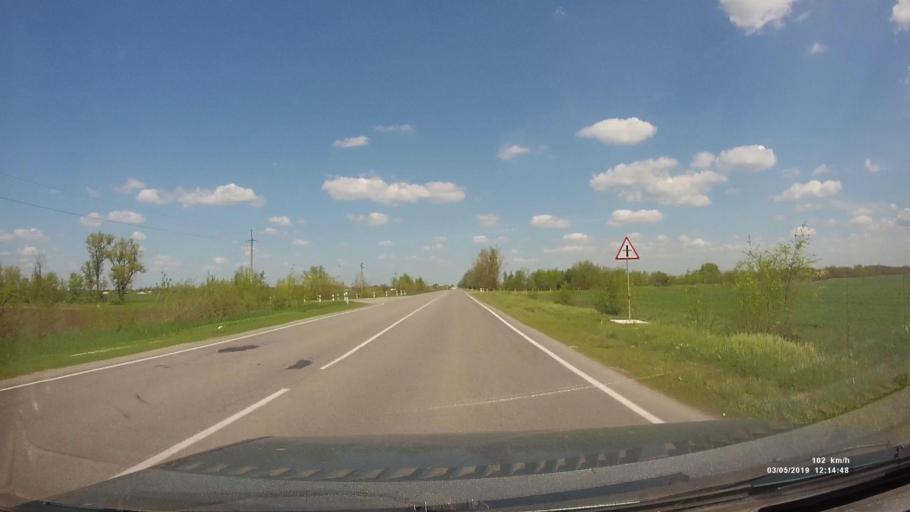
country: RU
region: Rostov
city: Melikhovskaya
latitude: 47.3490
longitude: 40.5672
